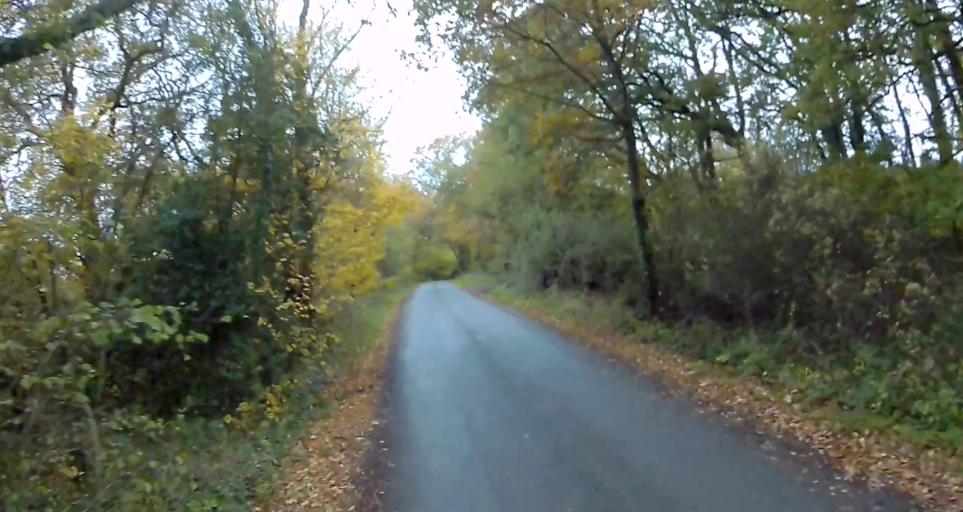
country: GB
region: England
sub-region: Hampshire
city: Odiham
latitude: 51.2467
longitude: -0.9037
